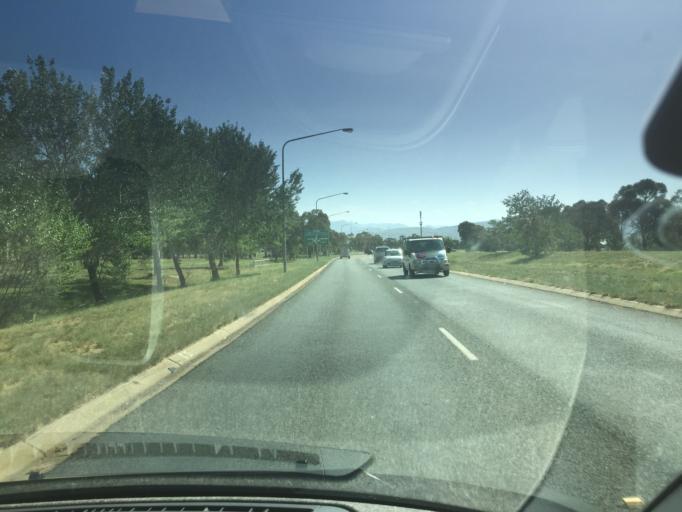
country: AU
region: Australian Capital Territory
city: Macarthur
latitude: -35.4222
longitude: 149.0935
